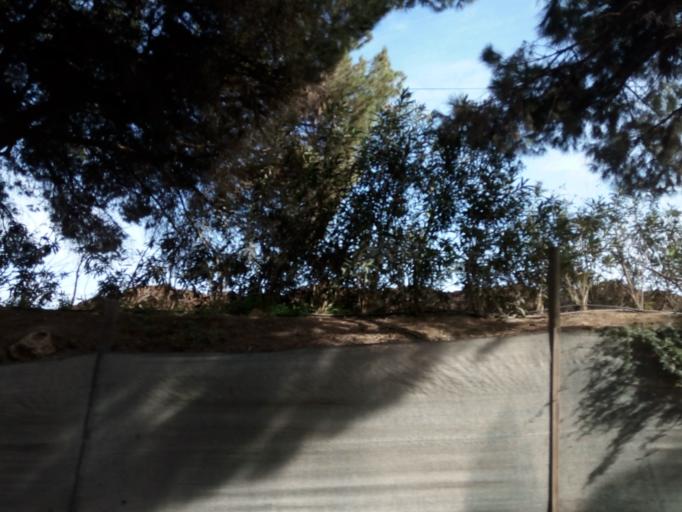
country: PT
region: Faro
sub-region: Faro
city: Faro
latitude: 37.0330
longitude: -7.9785
